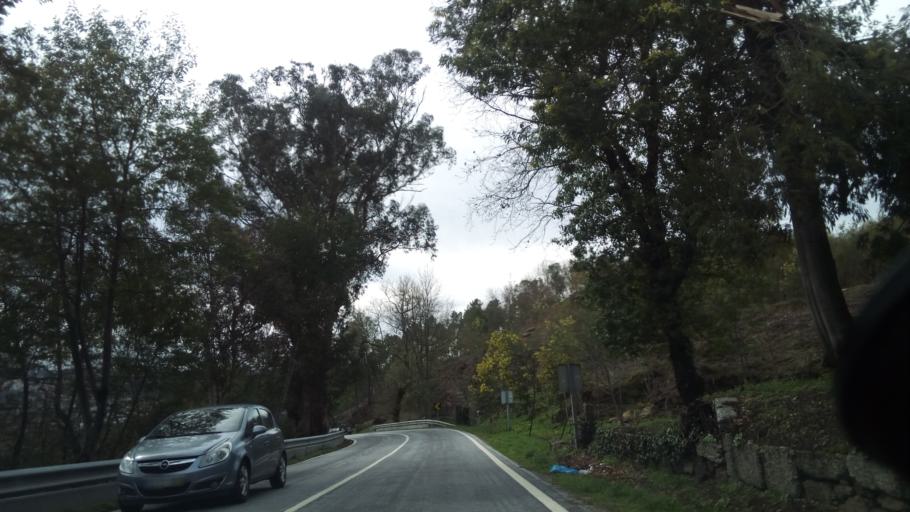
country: PT
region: Guarda
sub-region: Seia
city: Seia
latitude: 40.4390
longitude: -7.7093
